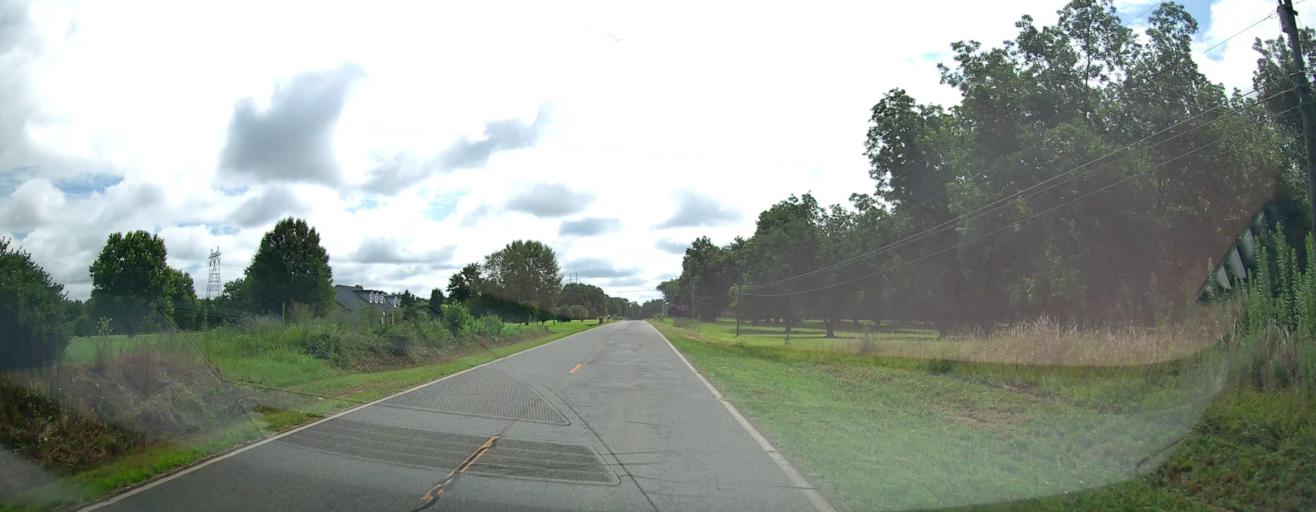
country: US
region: Georgia
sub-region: Peach County
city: Byron
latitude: 32.6454
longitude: -83.7812
